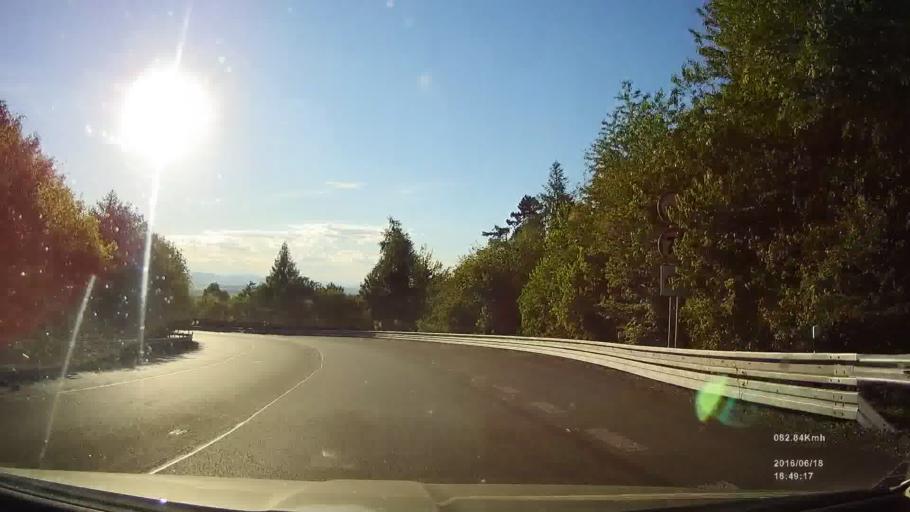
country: SK
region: Kosicky
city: Secovce
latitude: 48.7432
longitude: 21.5300
